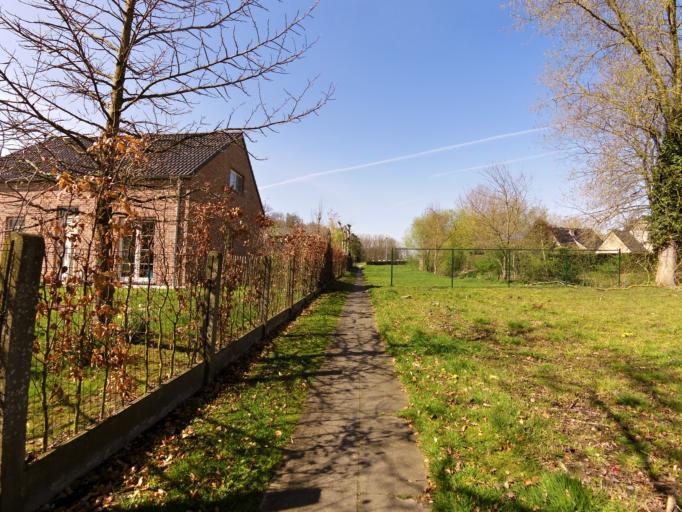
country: BE
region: Flanders
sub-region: Provincie West-Vlaanderen
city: Jabbeke
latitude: 51.1864
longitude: 3.0902
